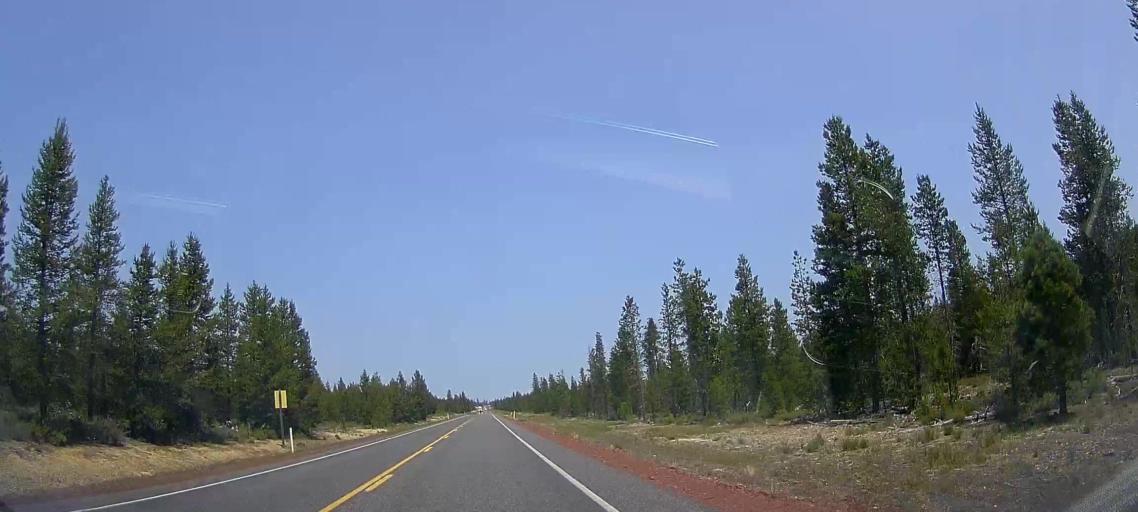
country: US
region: Oregon
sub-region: Deschutes County
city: La Pine
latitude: 43.3876
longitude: -121.7290
